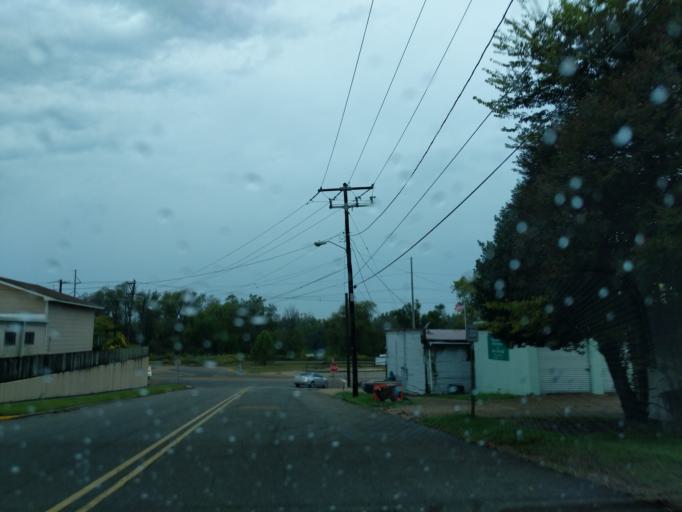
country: US
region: Mississippi
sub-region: Warren County
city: Vicksburg
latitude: 32.3550
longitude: -90.8805
